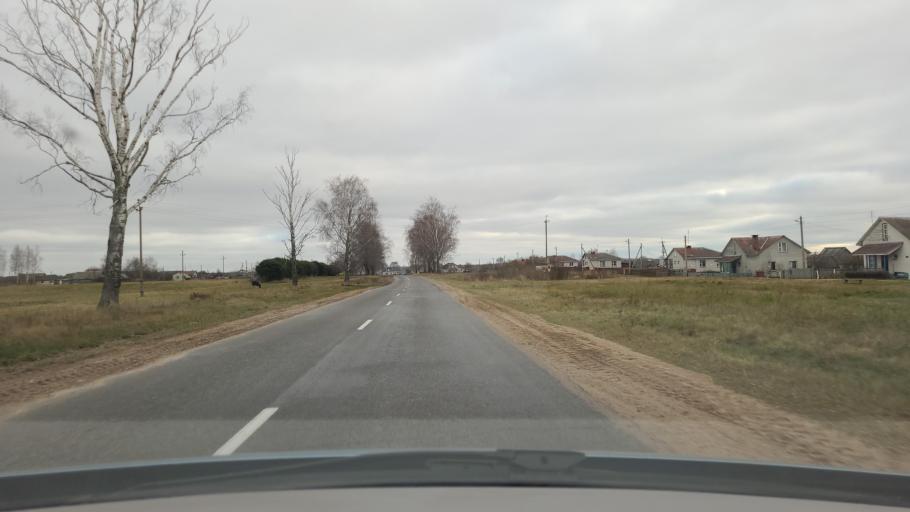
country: BY
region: Minsk
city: Khalopyenichy
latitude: 54.4718
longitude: 28.9742
